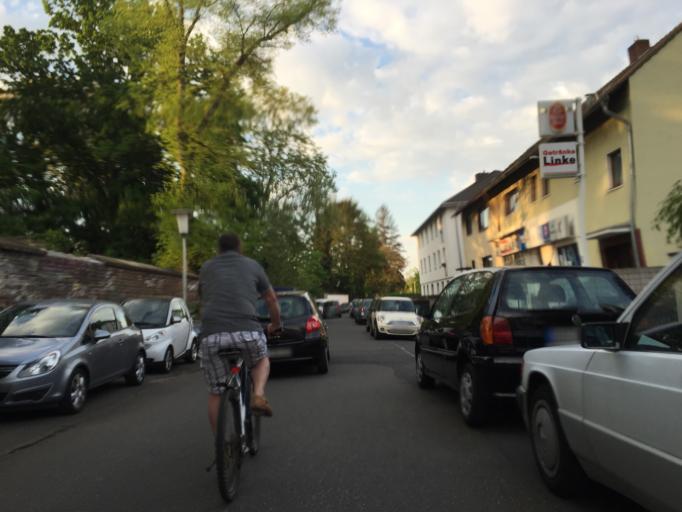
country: DE
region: North Rhine-Westphalia
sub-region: Regierungsbezirk Koln
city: Bonn
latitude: 50.7226
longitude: 7.0845
